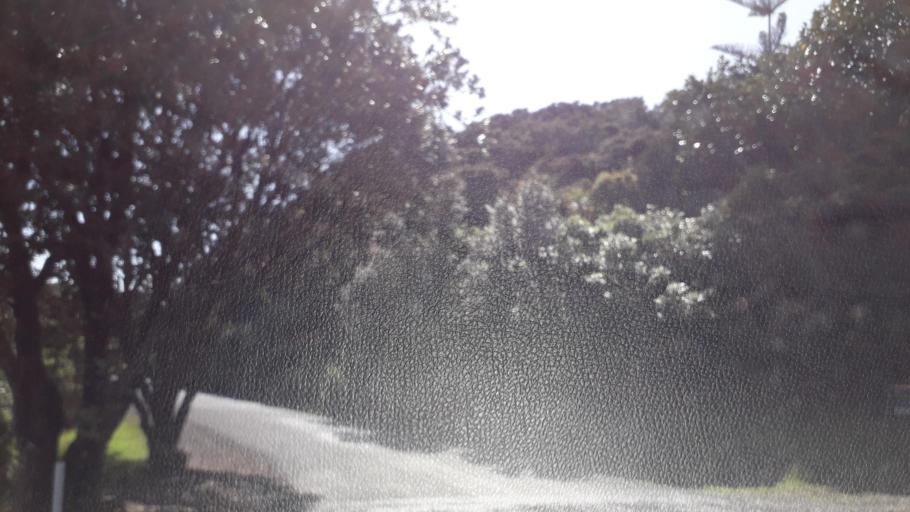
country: NZ
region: Northland
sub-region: Far North District
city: Paihia
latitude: -35.2281
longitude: 174.2633
